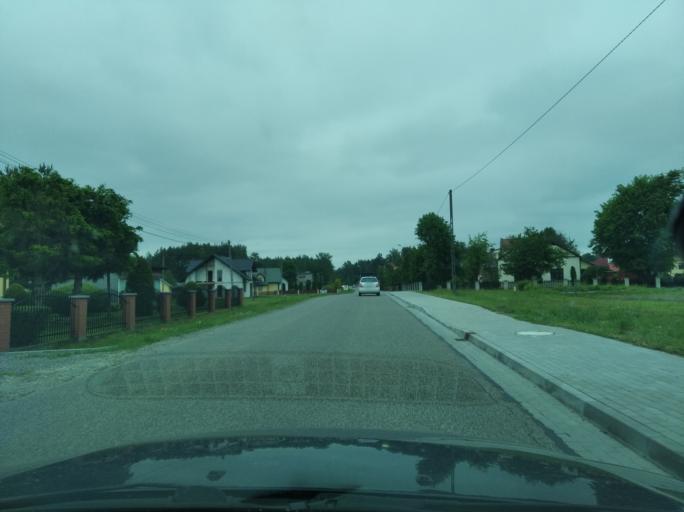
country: PL
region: Subcarpathian Voivodeship
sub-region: Powiat ropczycko-sedziszowski
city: Sedziszow Malopolski
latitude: 50.1397
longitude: 21.6696
